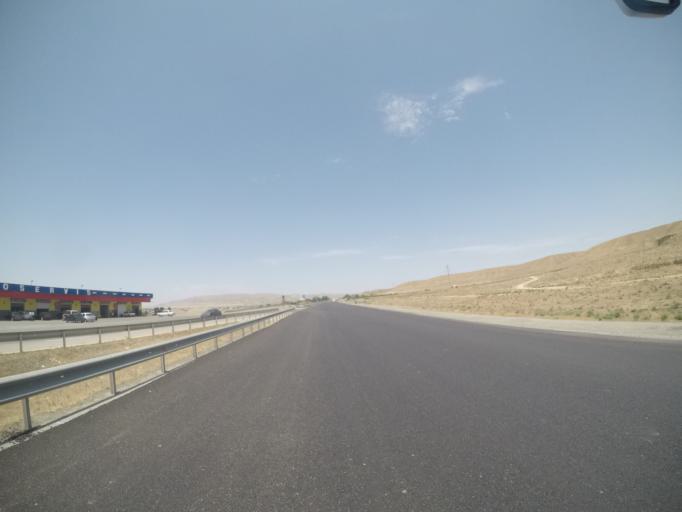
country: AZ
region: Haciqabul
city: Haciqabul
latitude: 40.0199
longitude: 48.9555
